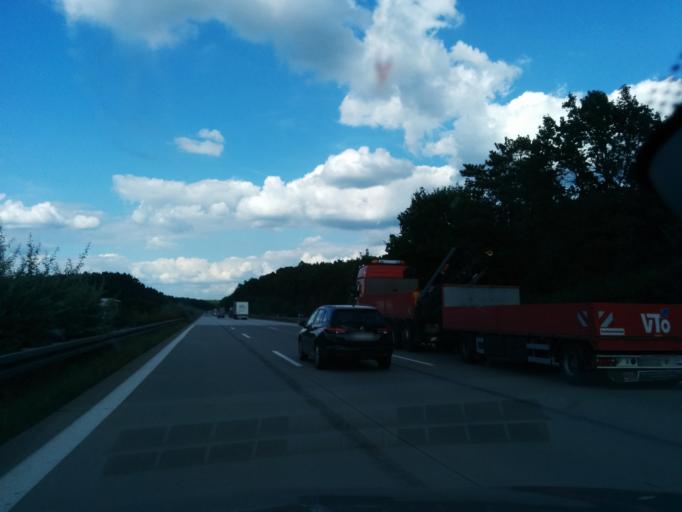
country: DE
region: Brandenburg
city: Erkner
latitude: 52.3530
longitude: 13.7582
